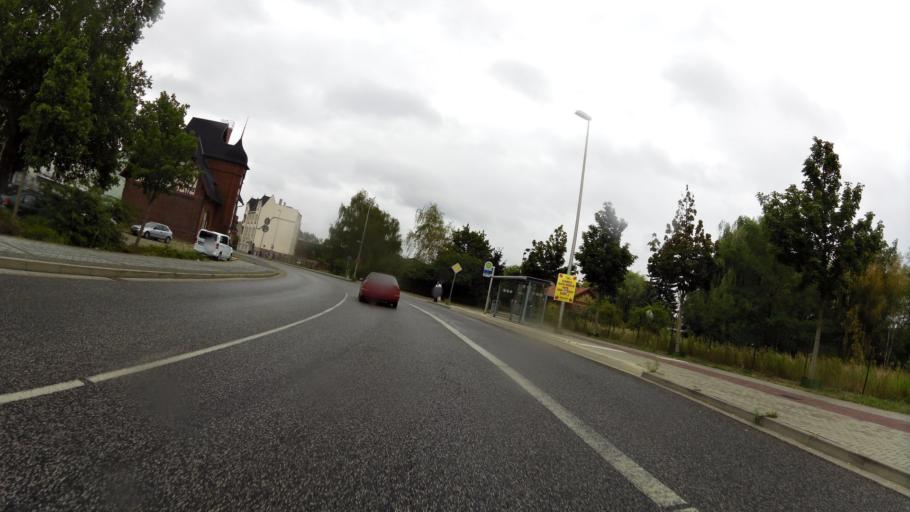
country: DE
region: Brandenburg
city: Cottbus
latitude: 51.7535
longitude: 14.3227
